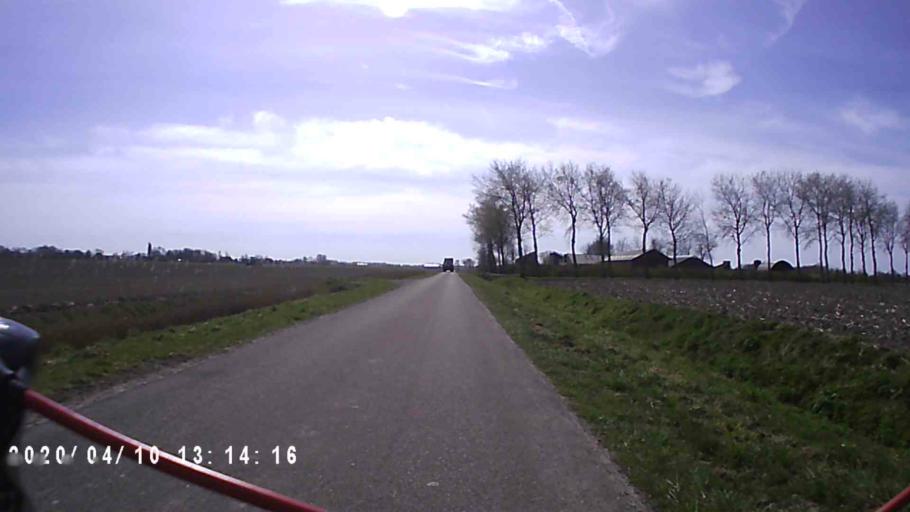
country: NL
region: Groningen
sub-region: Gemeente De Marne
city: Ulrum
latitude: 53.4010
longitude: 6.4175
